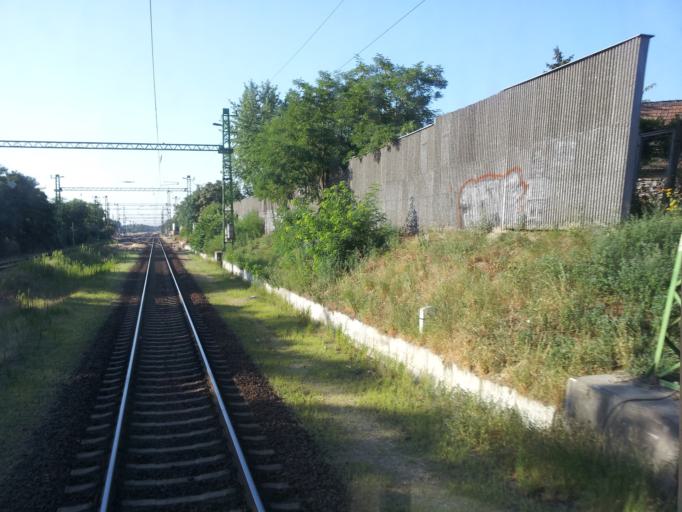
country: HU
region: Budapest
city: Budapest XXIII. keruelet
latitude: 47.4101
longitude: 19.1176
